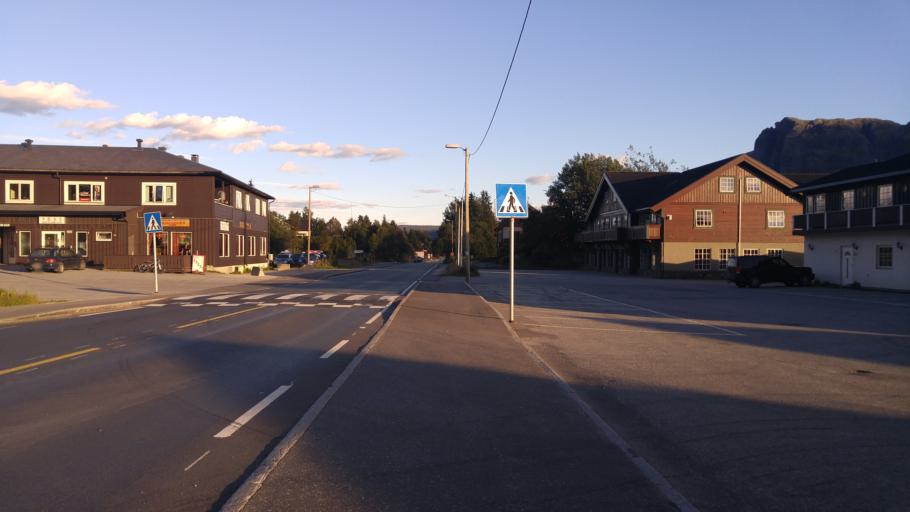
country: NO
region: Buskerud
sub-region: Hemsedal
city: Troim
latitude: 60.8500
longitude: 8.6160
